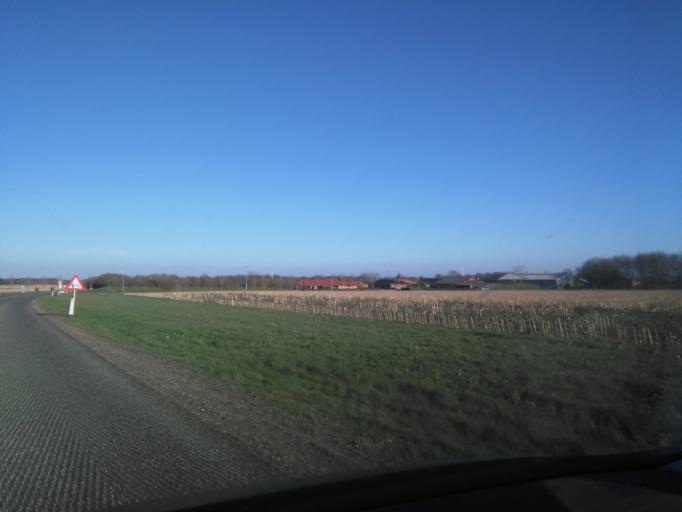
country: DK
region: Central Jutland
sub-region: Ringkobing-Skjern Kommune
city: Videbaek
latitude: 56.0988
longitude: 8.6292
